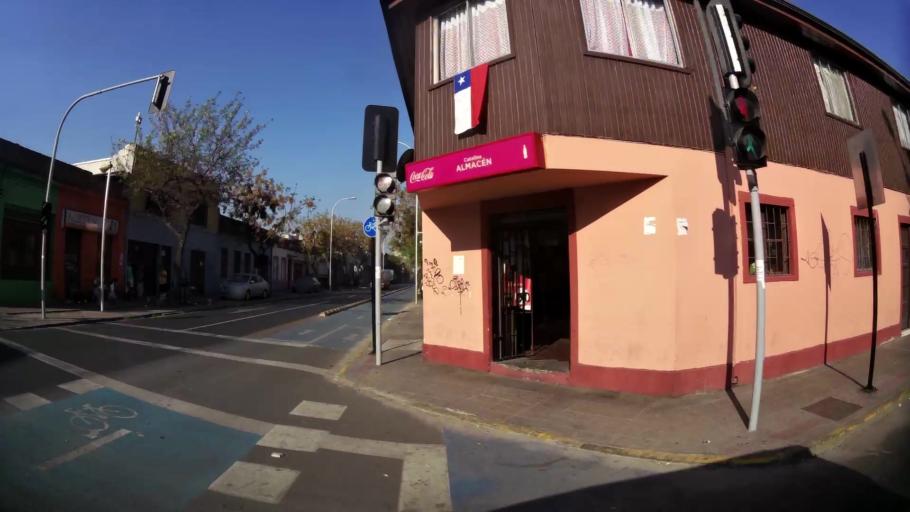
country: CL
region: Santiago Metropolitan
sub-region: Provincia de Santiago
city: Santiago
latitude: -33.4368
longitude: -70.6706
